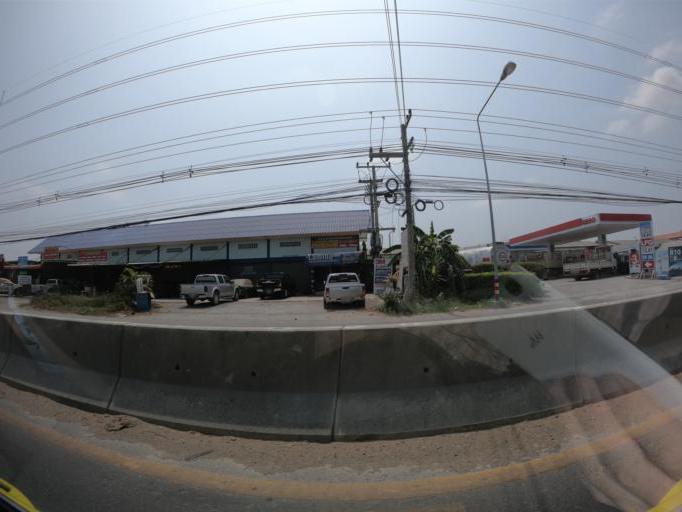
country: TH
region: Pathum Thani
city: Ban Lam Luk Ka
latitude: 13.9455
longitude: 100.7787
